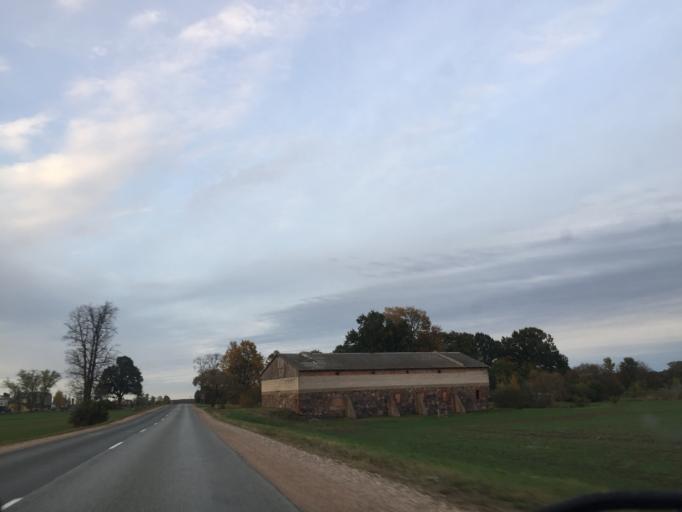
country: LV
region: Dobeles Rajons
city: Dobele
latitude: 56.7179
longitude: 23.3838
